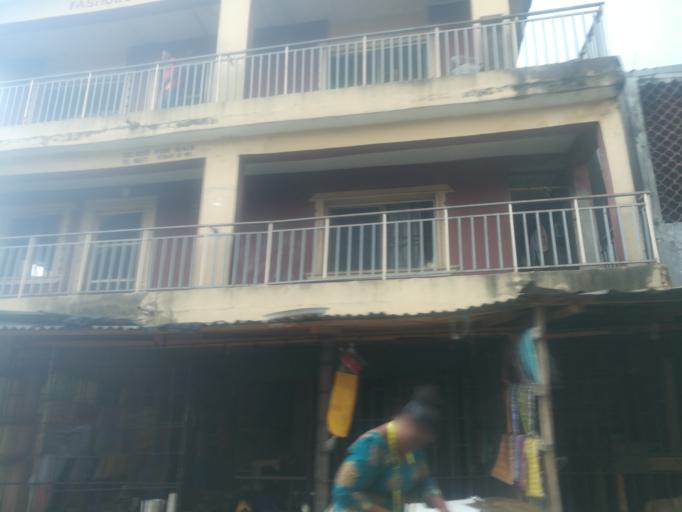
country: NG
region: Lagos
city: Ojota
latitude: 6.5935
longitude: 3.3857
